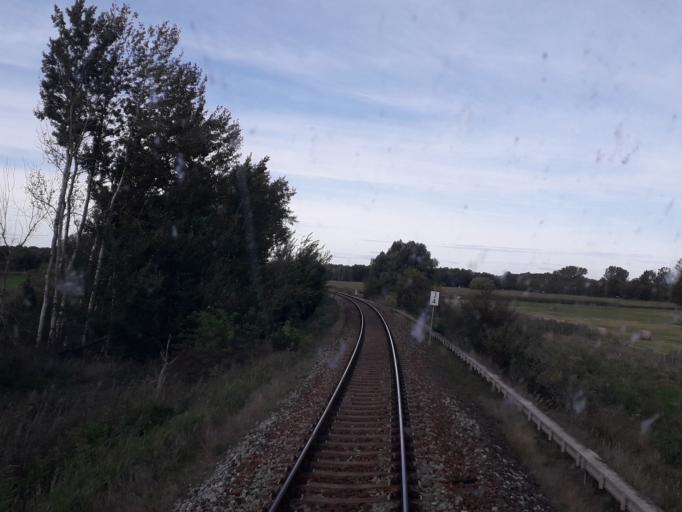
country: DE
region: Brandenburg
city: Kremmen
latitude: 52.7782
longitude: 13.0408
